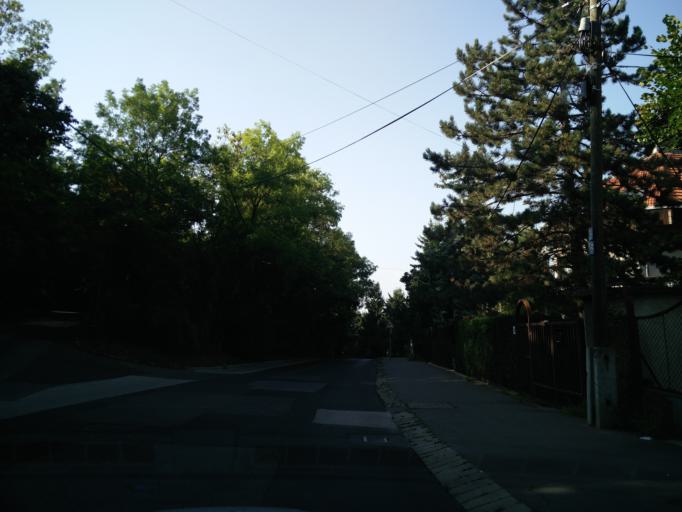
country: HU
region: Budapest
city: Budapest XII. keruelet
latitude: 47.5049
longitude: 18.9826
